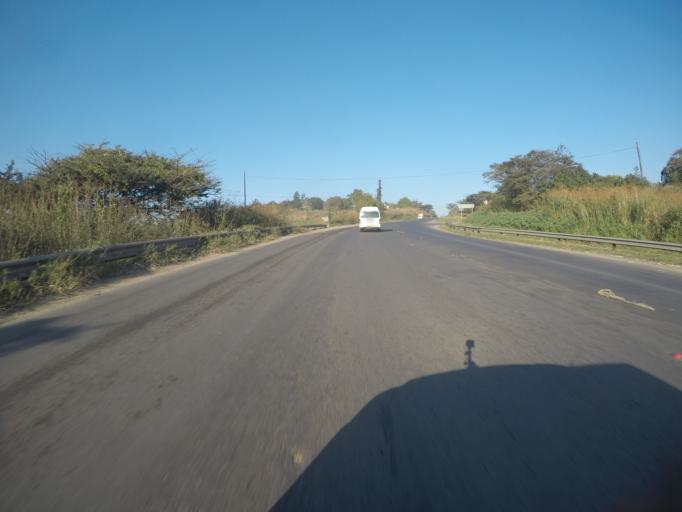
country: ZA
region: KwaZulu-Natal
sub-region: iLembe District Municipality
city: Stanger
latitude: -29.3861
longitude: 31.2534
